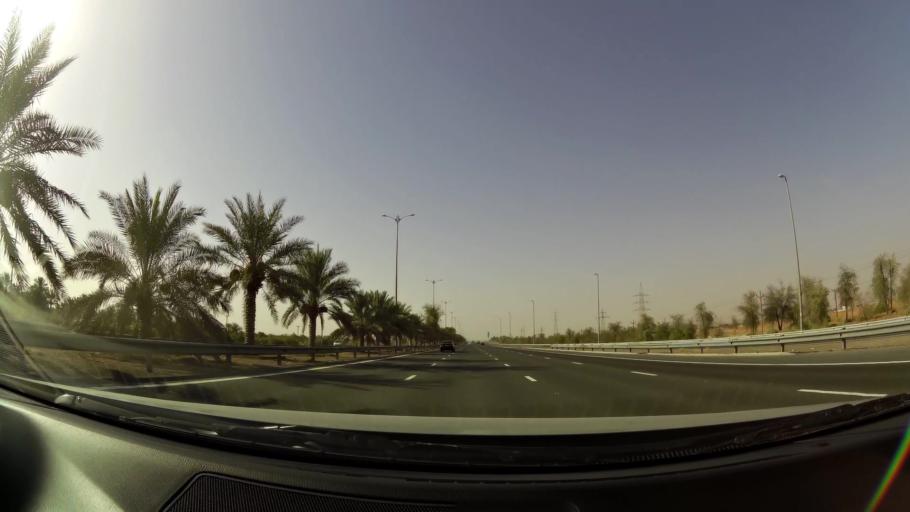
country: OM
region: Al Buraimi
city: Al Buraymi
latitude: 24.4797
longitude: 55.7748
